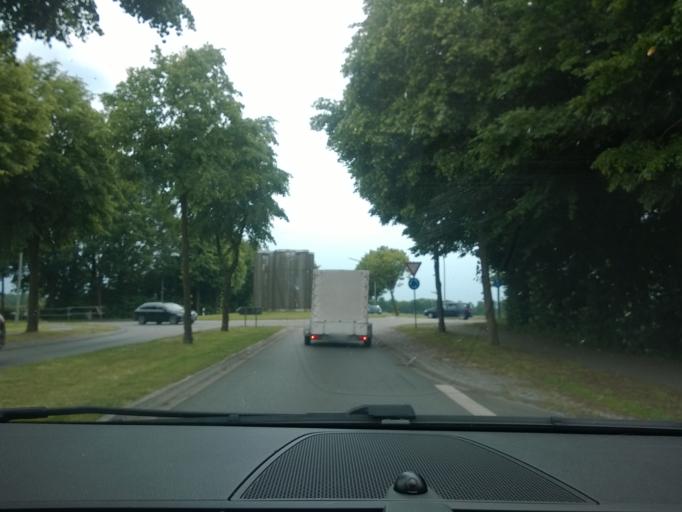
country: DE
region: North Rhine-Westphalia
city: Stadtlohn
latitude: 51.9823
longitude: 6.9057
